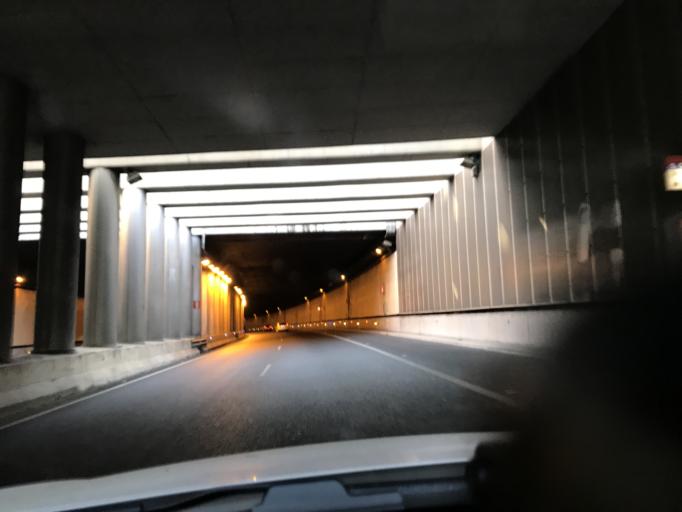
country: ES
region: Andalusia
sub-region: Provincia de Malaga
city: Benahavis
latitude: 36.4845
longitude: -4.9850
